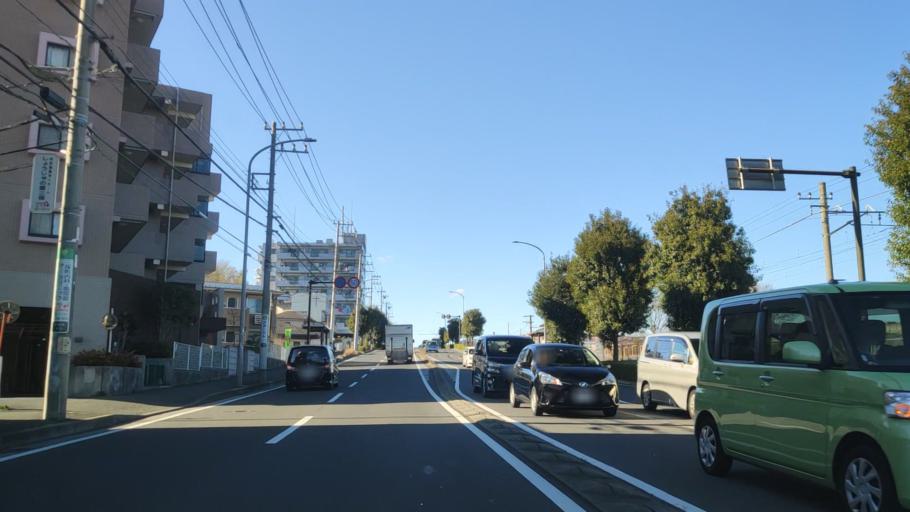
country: JP
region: Tokyo
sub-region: Machida-shi
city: Machida
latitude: 35.5199
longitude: 139.5288
